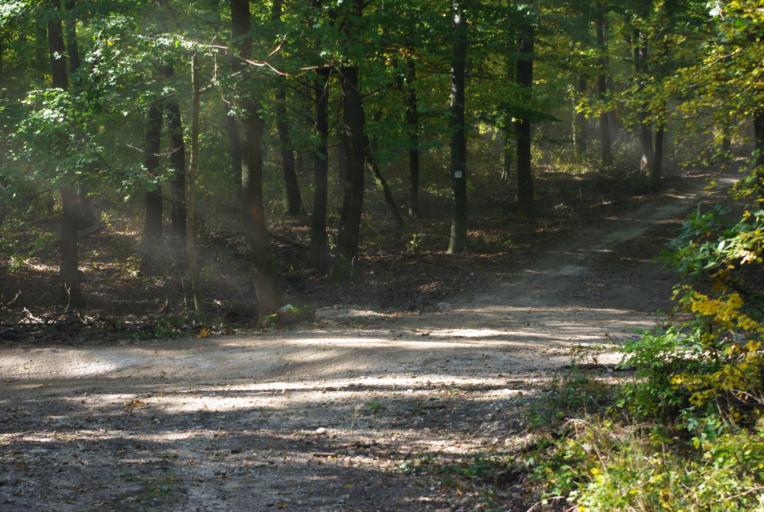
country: HU
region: Pest
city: Budakeszi
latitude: 47.5316
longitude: 18.9333
